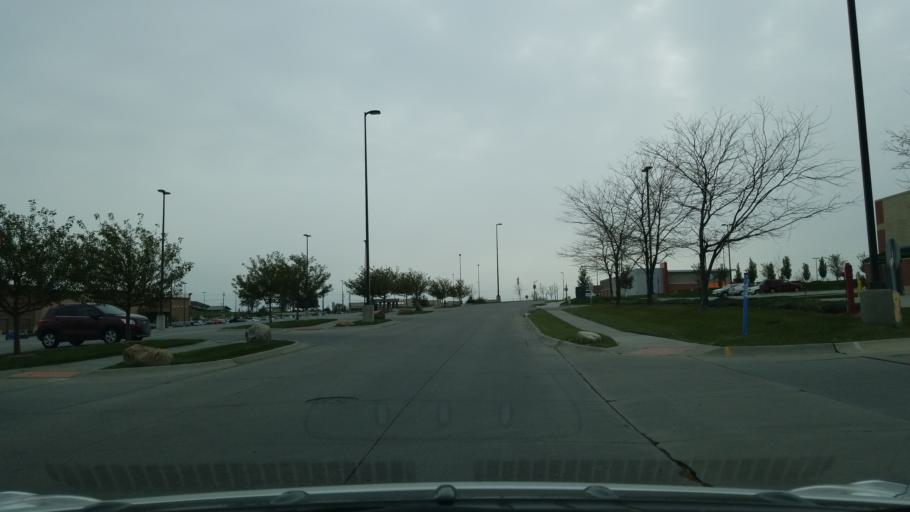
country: US
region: Nebraska
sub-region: Sarpy County
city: La Vista
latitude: 41.1647
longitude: -96.0223
